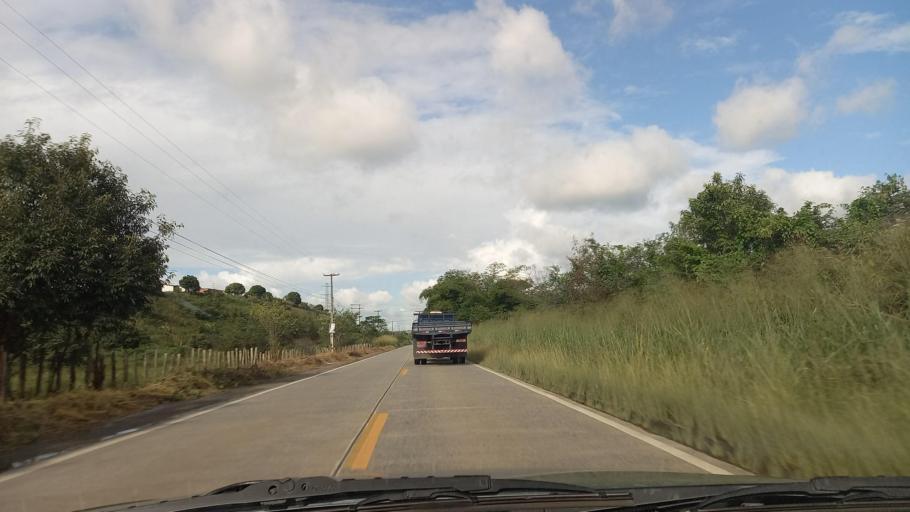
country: BR
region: Pernambuco
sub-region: Palmares
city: Palmares
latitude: -8.6913
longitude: -35.6210
